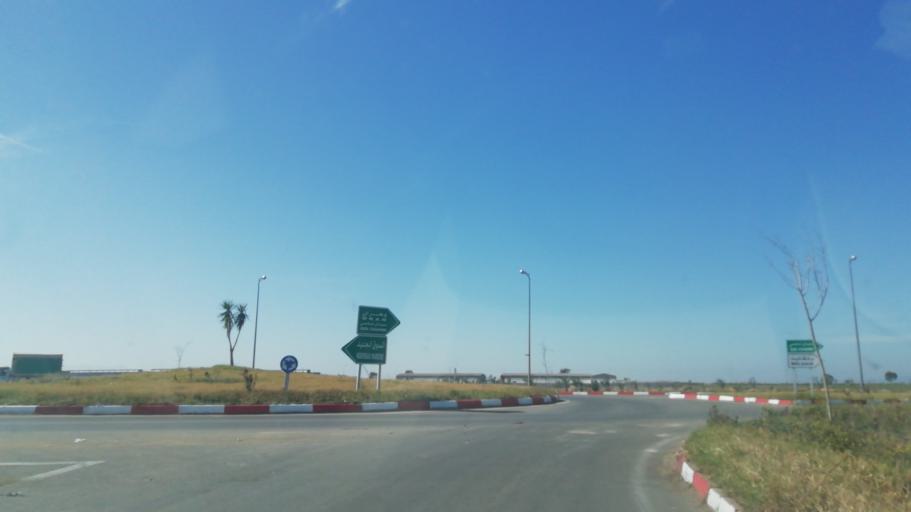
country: DZ
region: Oran
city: Es Senia
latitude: 35.5994
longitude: -0.5746
